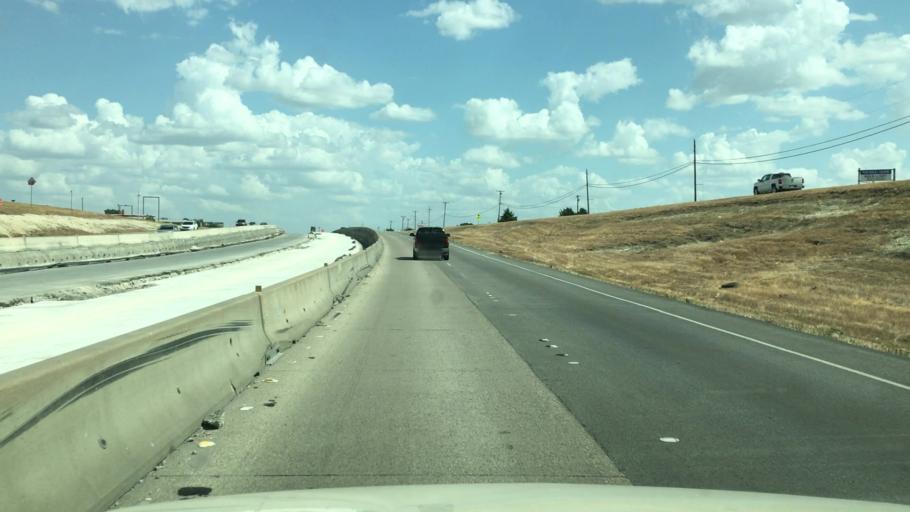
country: US
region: Texas
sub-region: Ellis County
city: Waxahachie
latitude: 32.3738
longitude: -96.8635
